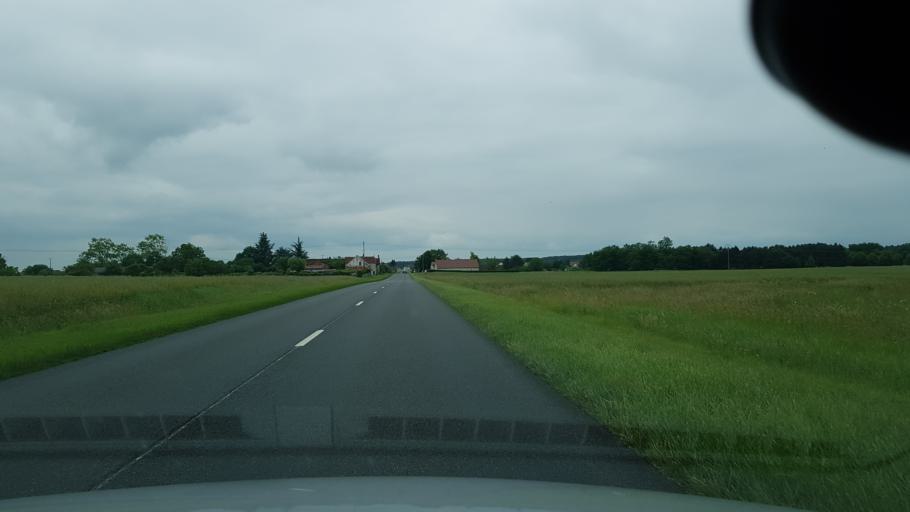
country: FR
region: Centre
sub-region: Departement du Loir-et-Cher
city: Chatillon-sur-Cher
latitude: 47.3123
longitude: 1.5027
